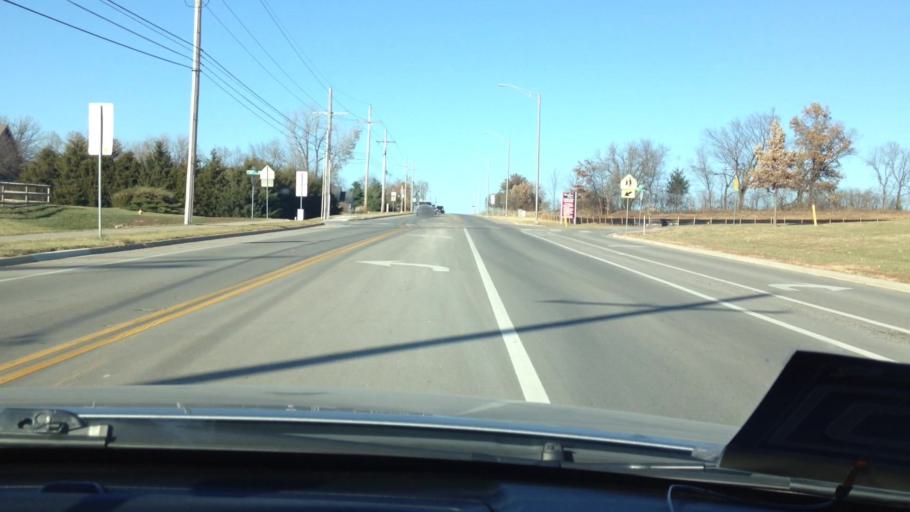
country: US
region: Kansas
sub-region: Johnson County
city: Olathe
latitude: 38.9186
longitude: -94.8160
